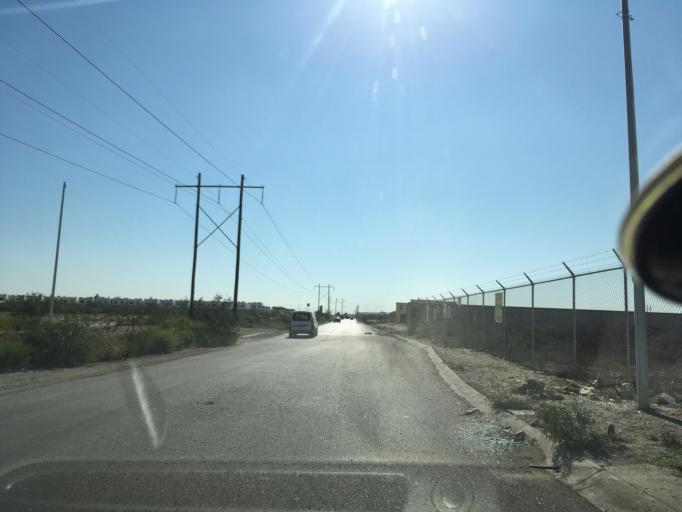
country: MX
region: Coahuila
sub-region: Torreon
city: Fraccionamiento la Noria
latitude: 25.5742
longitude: -103.3730
